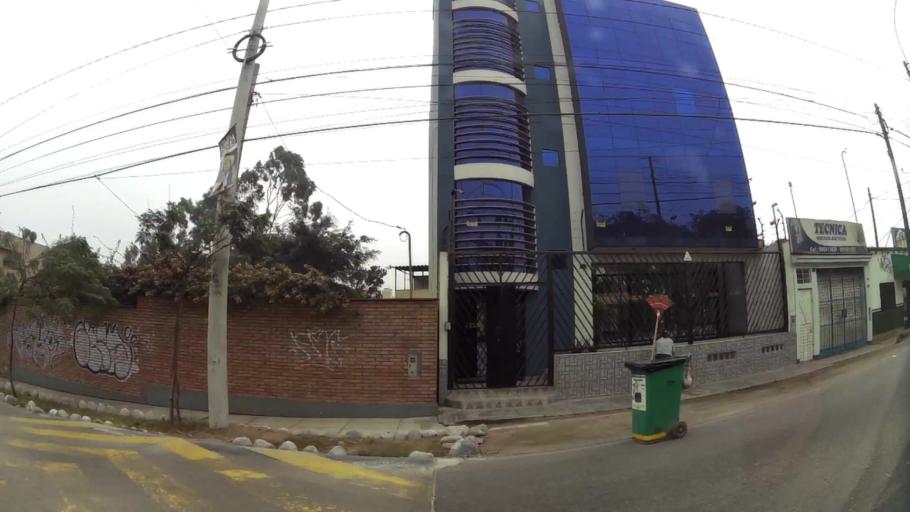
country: PE
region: Lima
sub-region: Lima
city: Chaclacayo
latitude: -11.9745
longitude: -76.7667
